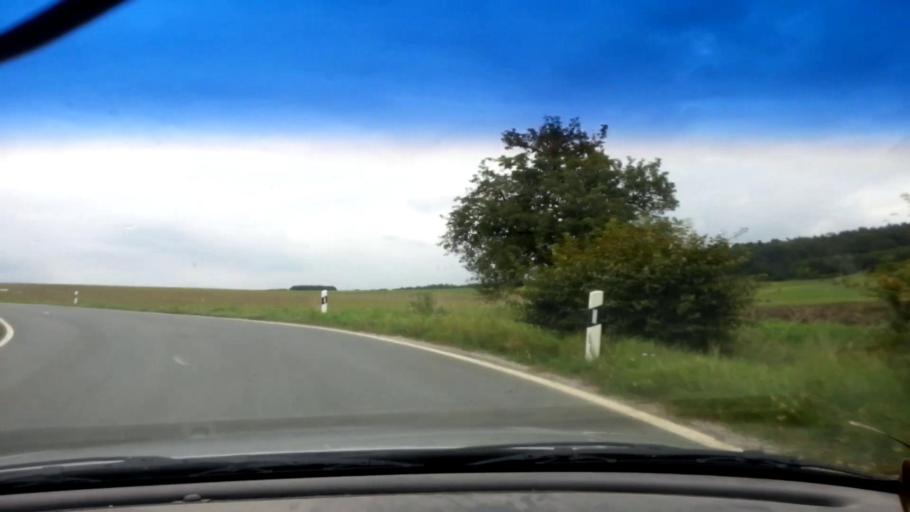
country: DE
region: Bavaria
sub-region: Upper Franconia
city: Litzendorf
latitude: 49.9377
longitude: 11.0166
